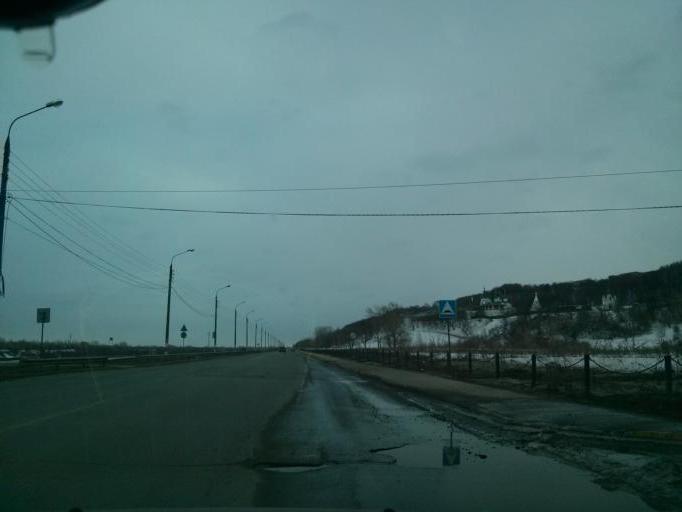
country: RU
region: Nizjnij Novgorod
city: Nizhniy Novgorod
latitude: 56.3270
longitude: 44.0420
